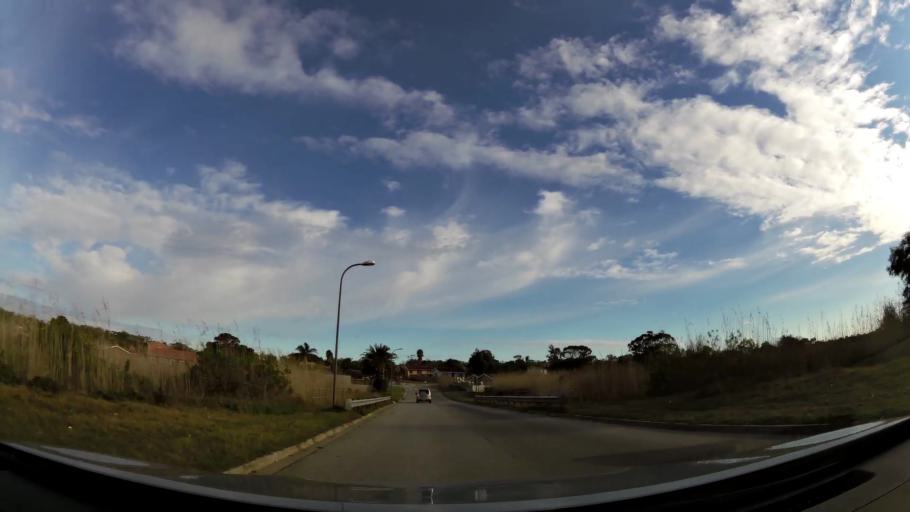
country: ZA
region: Eastern Cape
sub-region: Nelson Mandela Bay Metropolitan Municipality
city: Port Elizabeth
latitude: -33.9628
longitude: 25.4765
